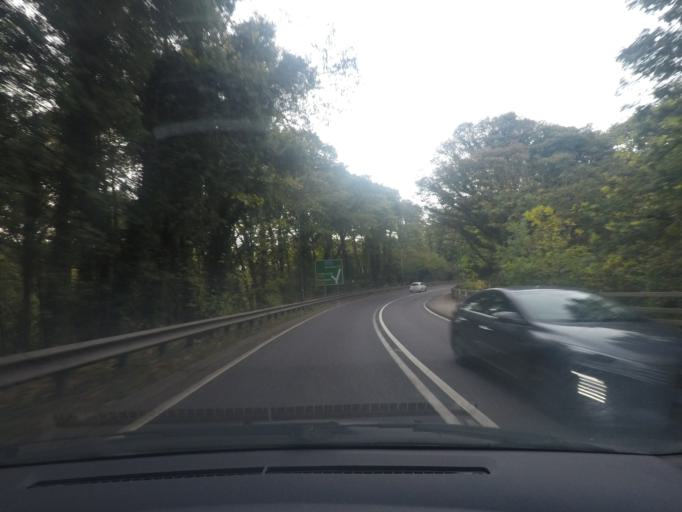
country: GB
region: England
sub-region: Barnsley
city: Wortley
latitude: 53.4663
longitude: -1.5071
